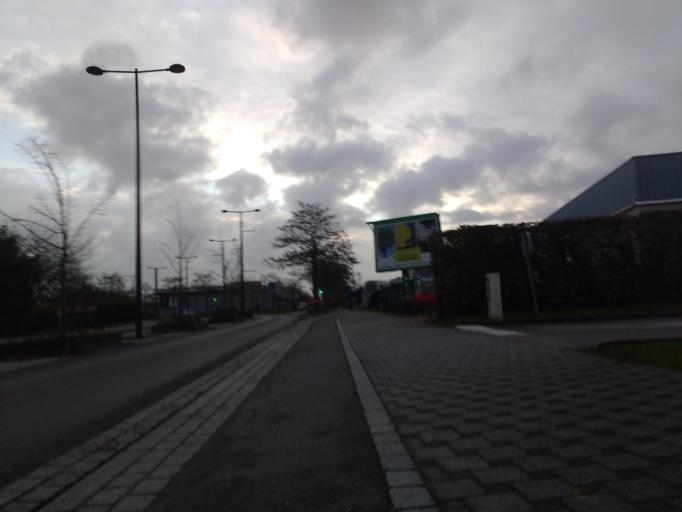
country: FR
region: Picardie
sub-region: Departement de la Somme
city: Longueau
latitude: 49.8681
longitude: 2.3634
